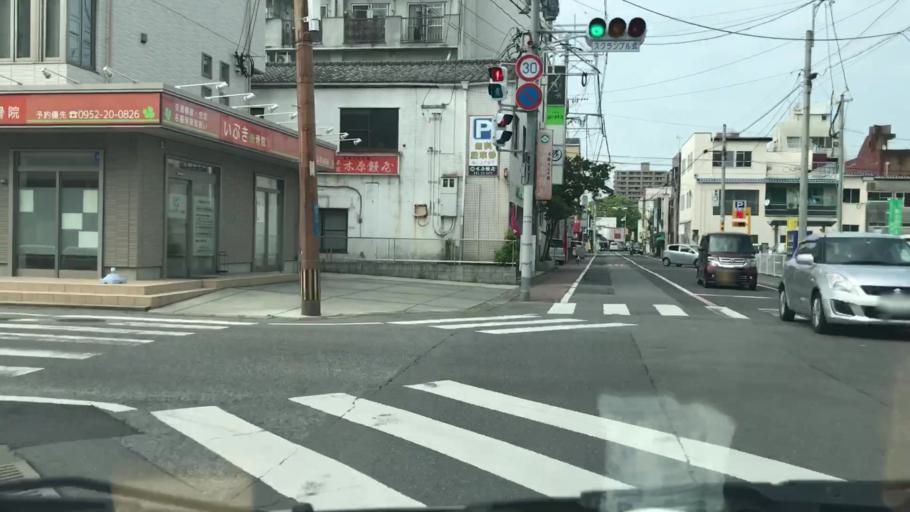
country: JP
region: Saga Prefecture
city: Saga-shi
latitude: 33.2525
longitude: 130.2992
